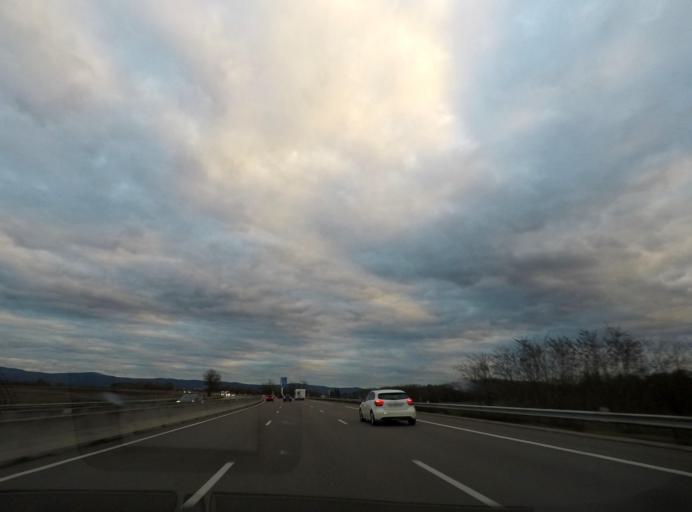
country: FR
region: Rhone-Alpes
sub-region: Departement de l'Ain
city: Saint-Martin-du-Mont
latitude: 46.0816
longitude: 5.2926
